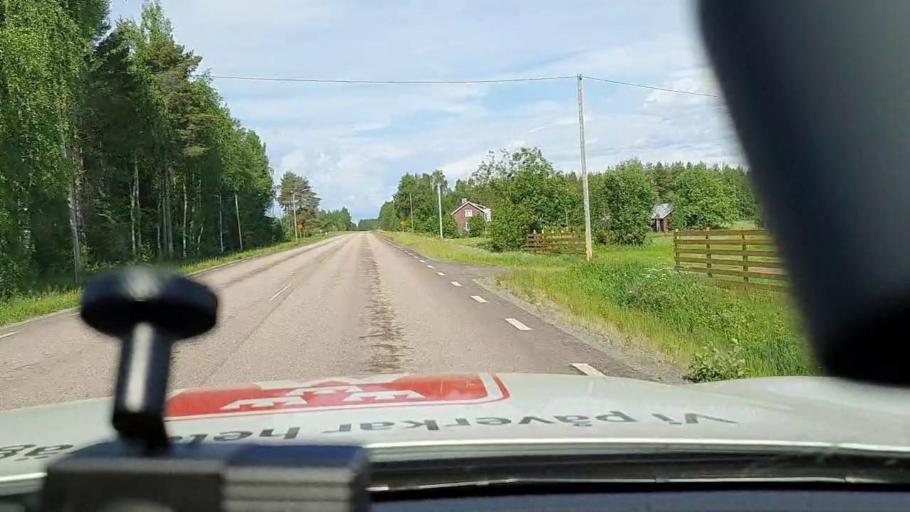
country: SE
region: Norrbotten
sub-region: Alvsbyns Kommun
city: AElvsbyn
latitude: 66.0174
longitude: 21.1514
